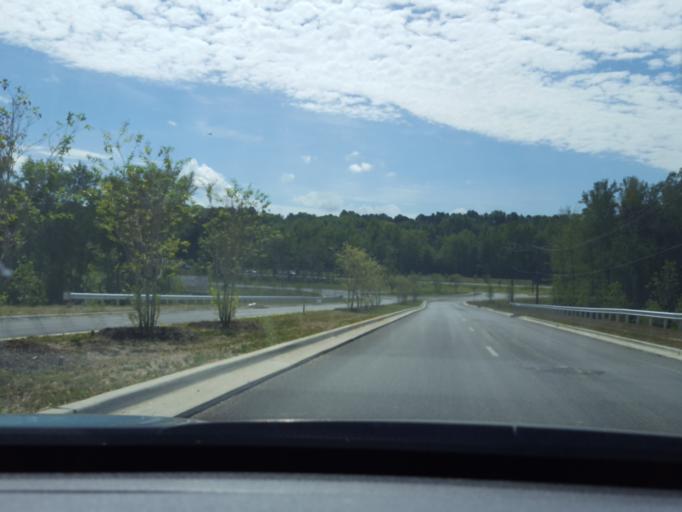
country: US
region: Maryland
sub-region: Prince George's County
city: Mellwood
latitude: 38.8189
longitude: -76.8338
